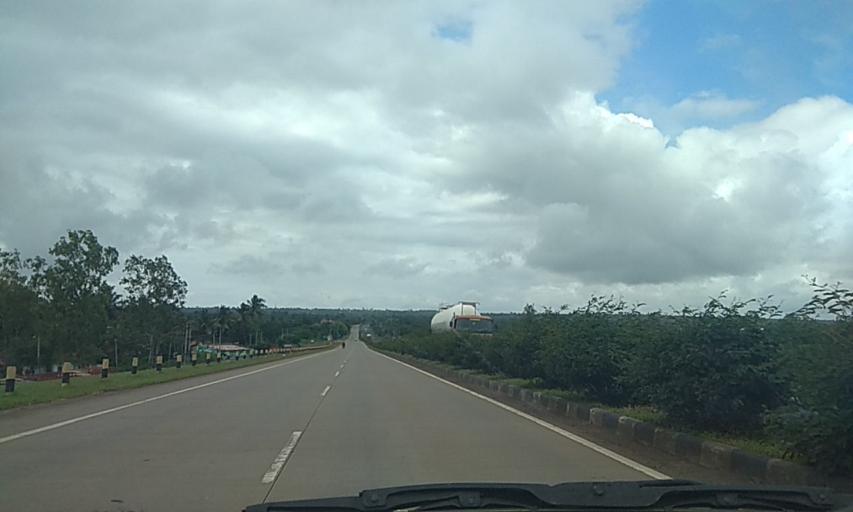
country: IN
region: Karnataka
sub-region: Belgaum
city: Sankeshwar
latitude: 16.3147
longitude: 74.4268
